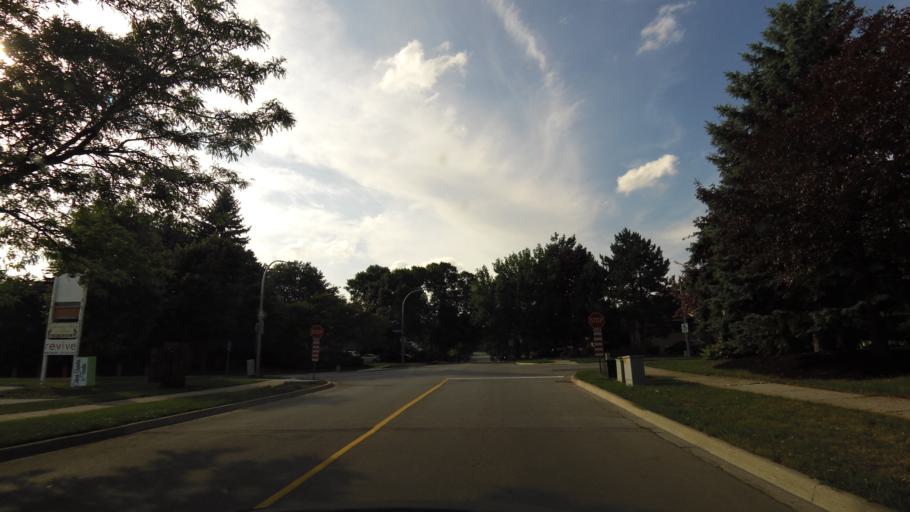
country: CA
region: Ontario
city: Burlington
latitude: 43.3411
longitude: -79.8379
